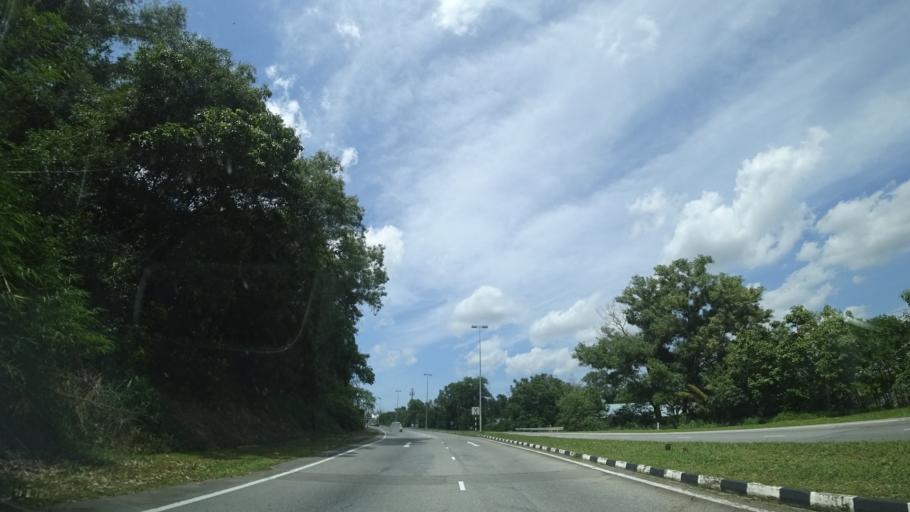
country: BN
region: Brunei and Muara
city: Bandar Seri Begawan
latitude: 4.8973
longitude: 114.9113
